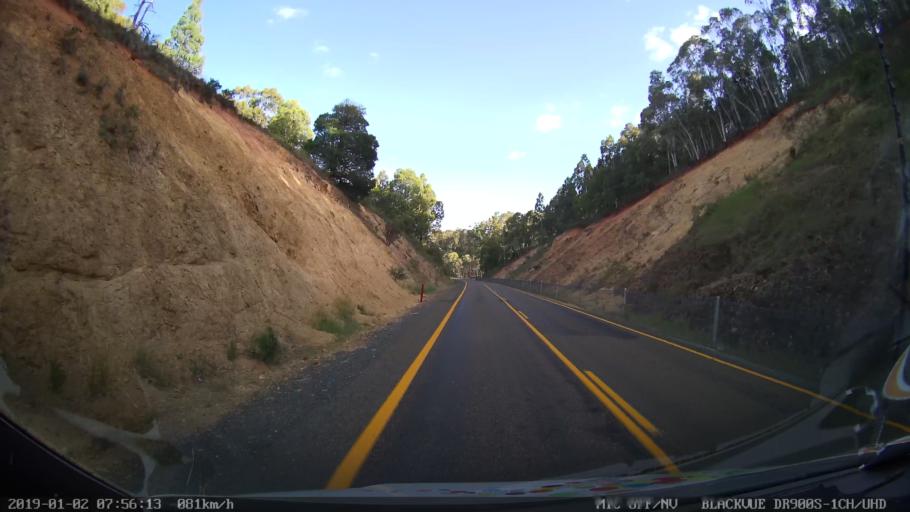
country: AU
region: New South Wales
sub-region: Tumut Shire
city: Tumut
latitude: -35.6734
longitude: 148.4859
